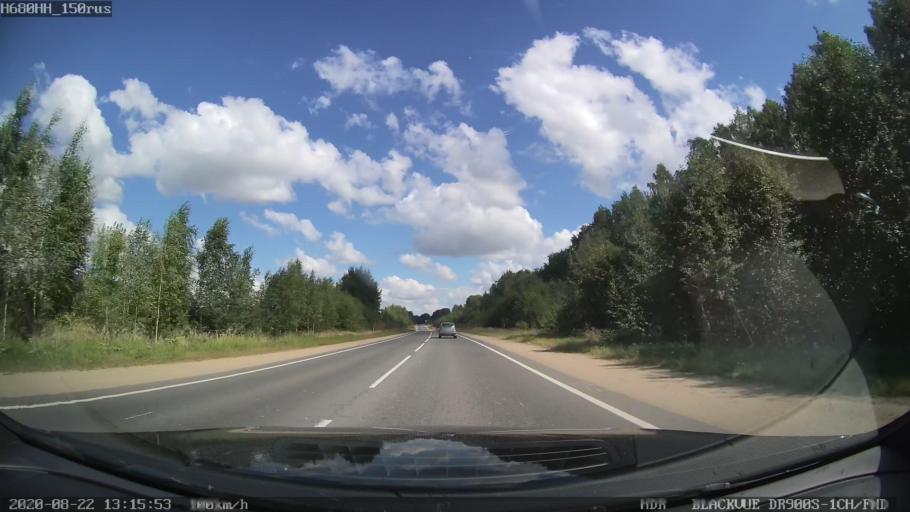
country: RU
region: Tverskaya
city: Bezhetsk
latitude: 57.7602
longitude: 36.6410
